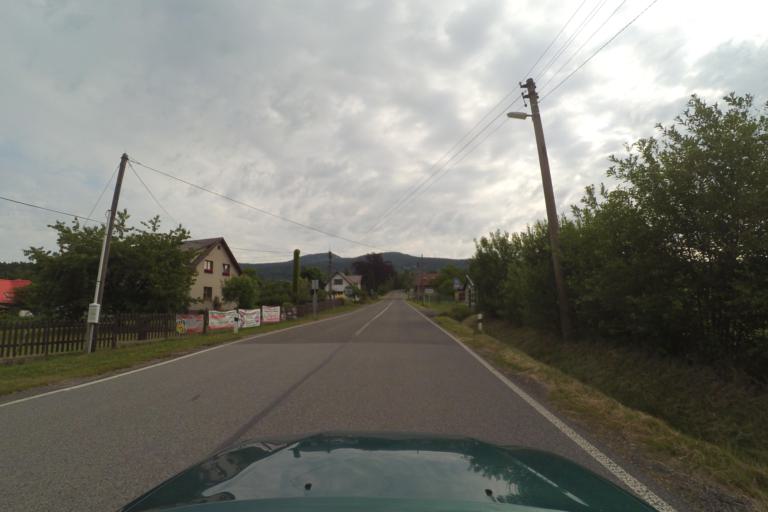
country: CZ
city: Osecna
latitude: 50.7088
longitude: 14.9668
